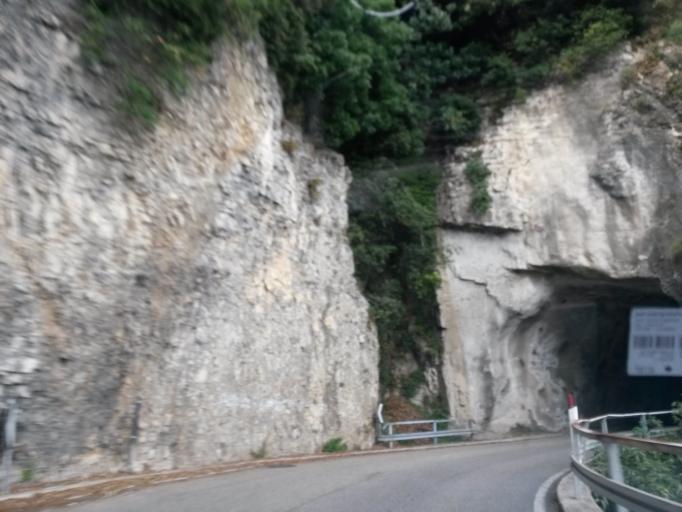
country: IT
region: Lombardy
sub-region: Provincia di Brescia
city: Gardola
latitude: 45.7234
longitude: 10.7083
